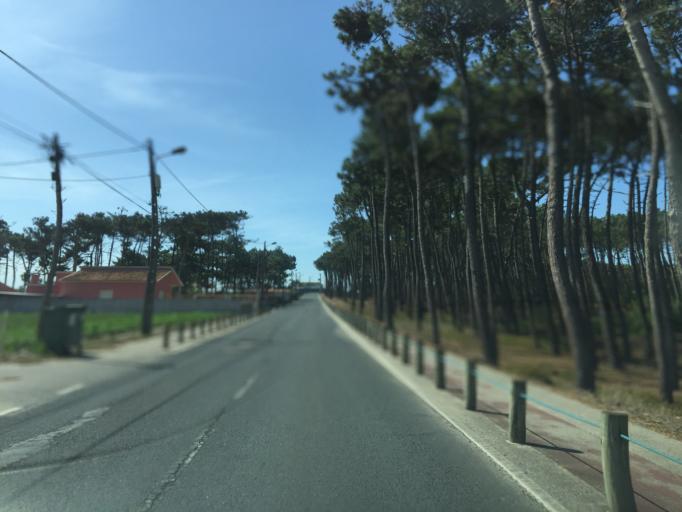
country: PT
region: Lisbon
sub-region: Torres Vedras
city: Silveira
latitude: 39.1566
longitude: -9.3612
